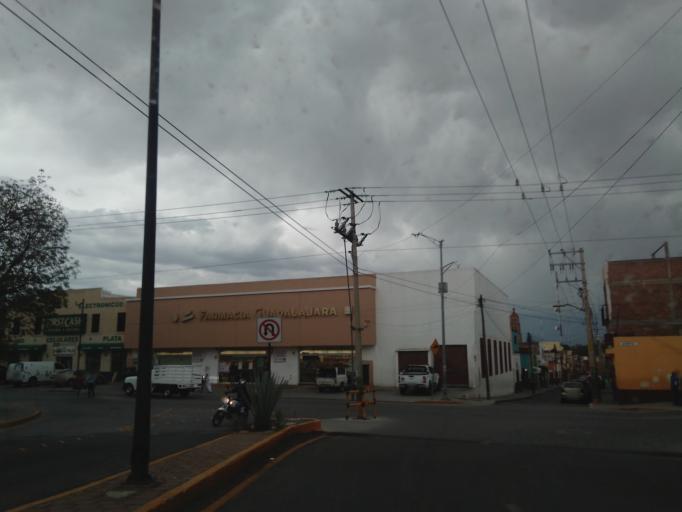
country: MX
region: Guanajuato
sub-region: Dolores Hidalgo Cuna de la Independencia Nacional
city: Colonia Padre Hidalgo
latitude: 21.1659
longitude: -100.9331
